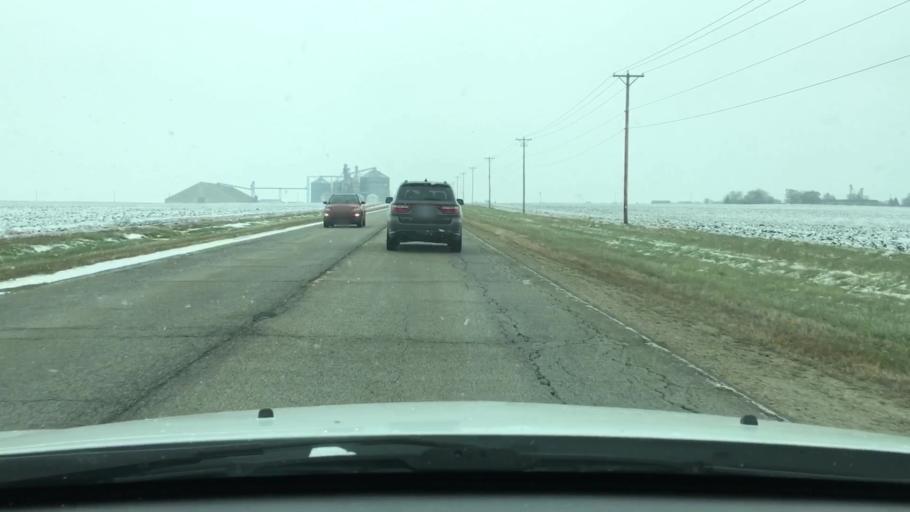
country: US
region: Illinois
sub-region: Ogle County
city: Hillcrest
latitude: 41.9350
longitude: -88.9800
